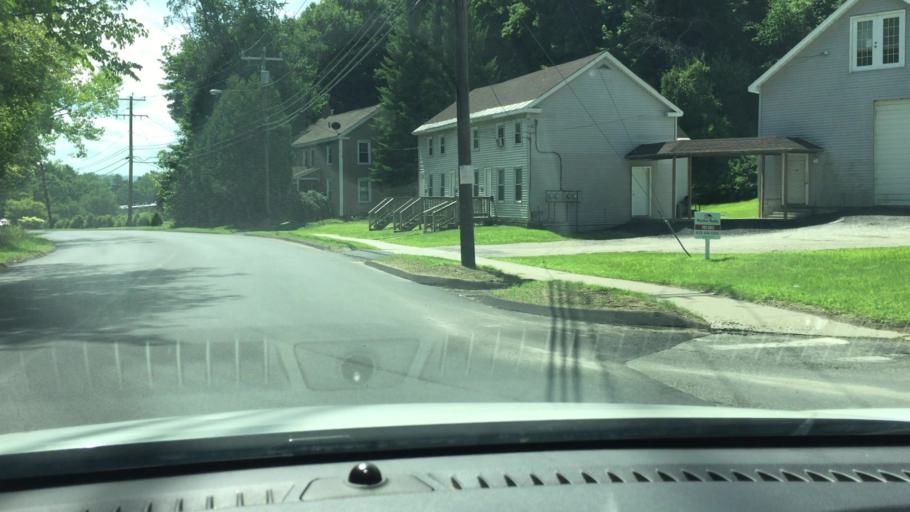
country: US
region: Massachusetts
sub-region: Berkshire County
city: Pittsfield
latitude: 42.4710
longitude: -73.2584
